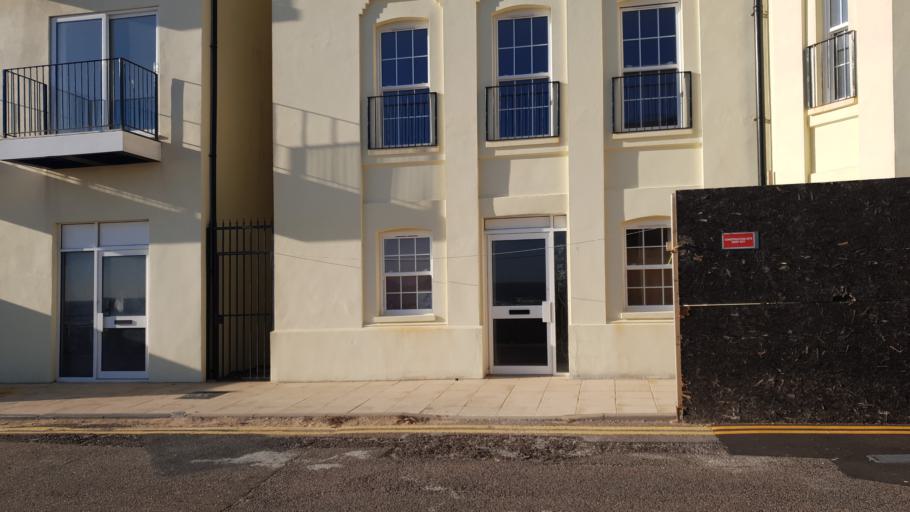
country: GB
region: England
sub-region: Essex
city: Walton-on-the-Naze
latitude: 51.8465
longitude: 1.2711
